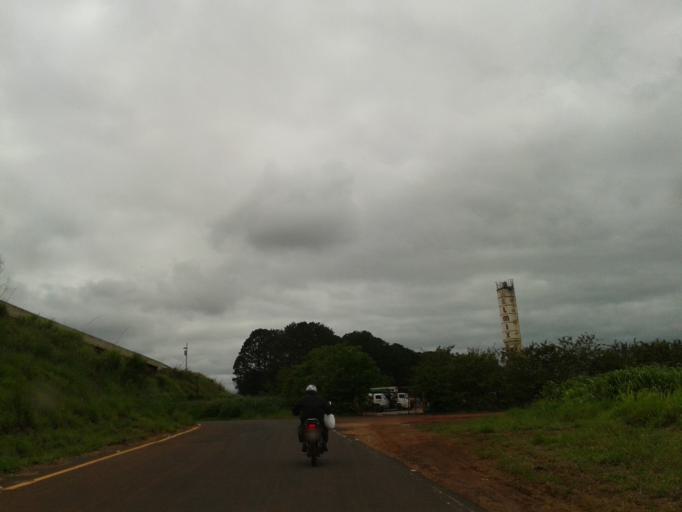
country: BR
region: Minas Gerais
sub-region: Uberlandia
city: Uberlandia
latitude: -18.9379
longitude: -48.2129
